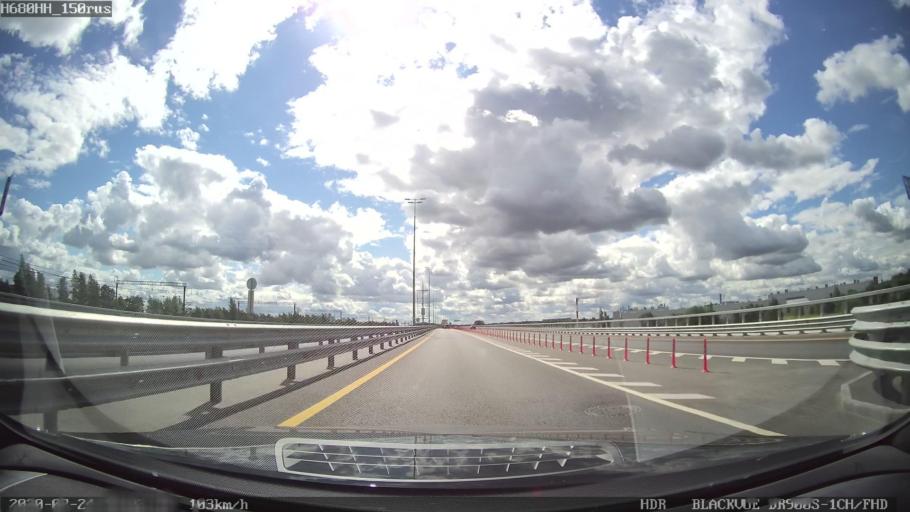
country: RU
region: St.-Petersburg
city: Shushary
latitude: 59.8045
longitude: 30.3352
